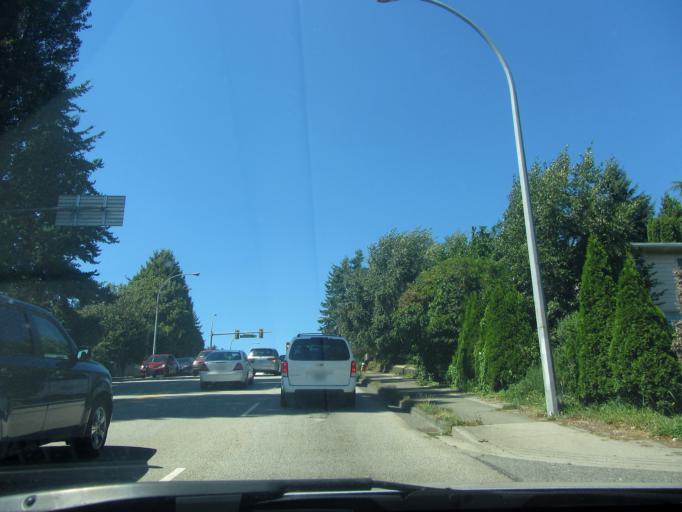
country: CA
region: British Columbia
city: New Westminster
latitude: 49.2010
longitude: -122.9459
